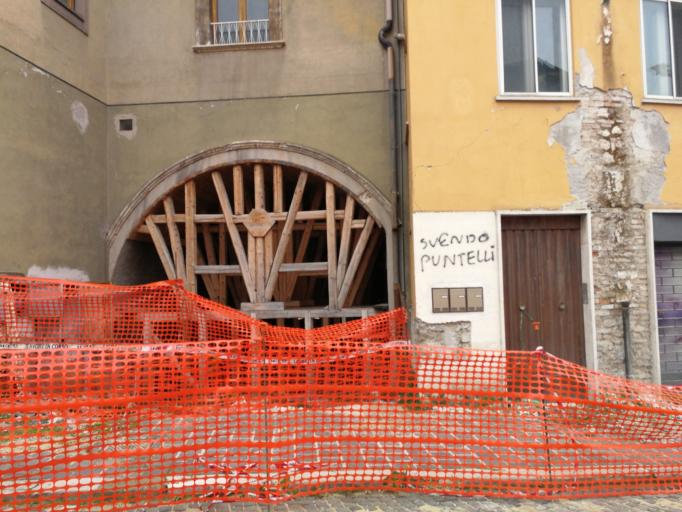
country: IT
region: Abruzzo
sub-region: Provincia dell' Aquila
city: L'Aquila
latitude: 42.3513
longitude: 13.3950
